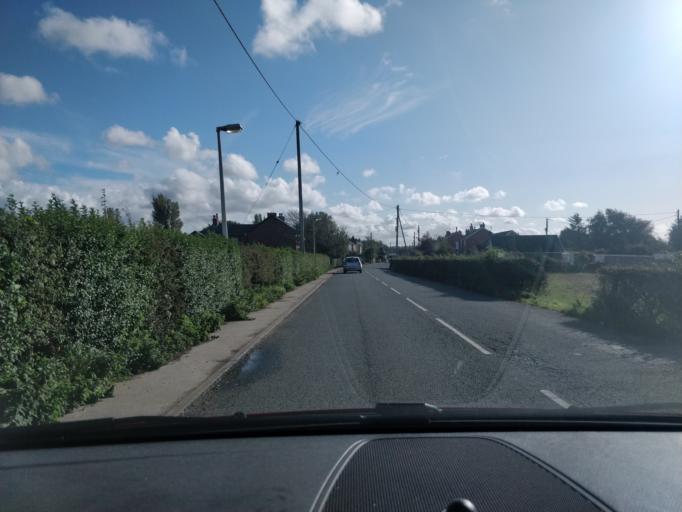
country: GB
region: England
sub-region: Lancashire
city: Banks
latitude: 53.6881
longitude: -2.9141
